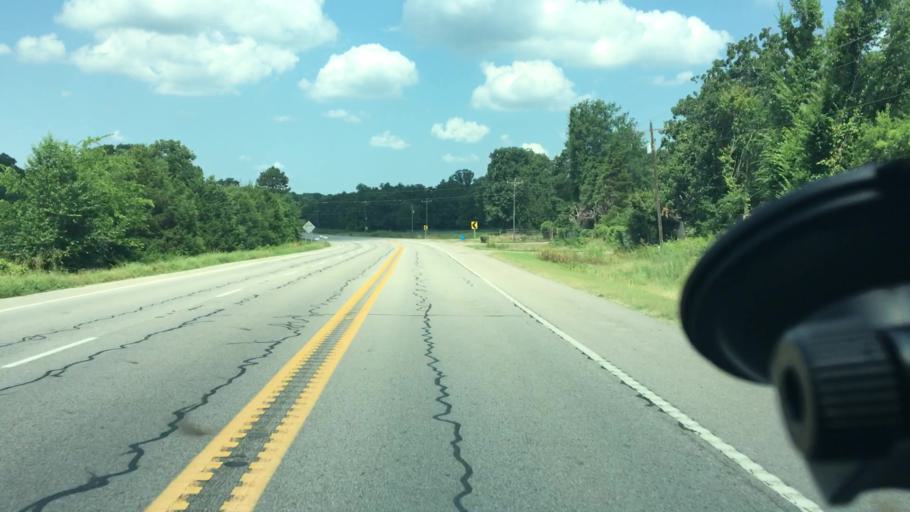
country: US
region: Arkansas
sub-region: Logan County
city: Paris
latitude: 35.2993
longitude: -93.8296
